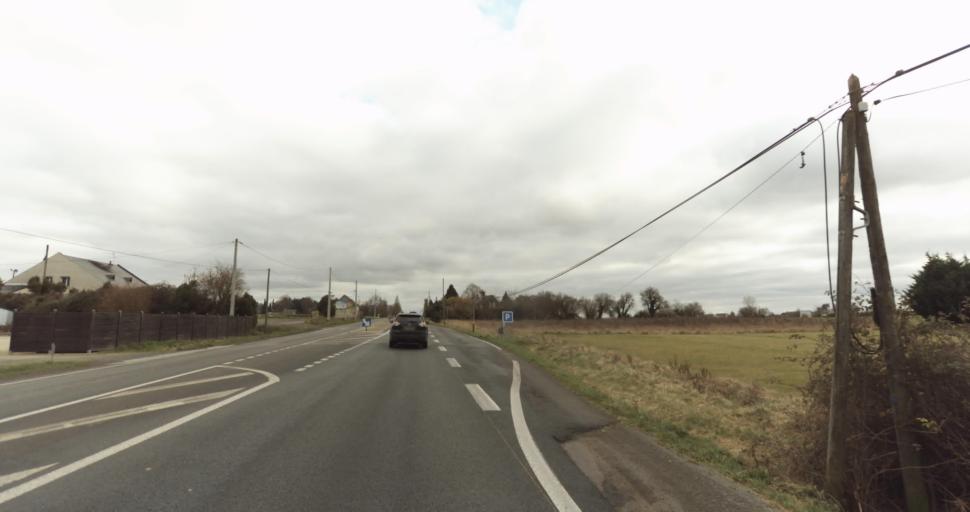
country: FR
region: Pays de la Loire
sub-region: Departement de Maine-et-Loire
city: Vivy
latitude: 47.3626
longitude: -0.0911
